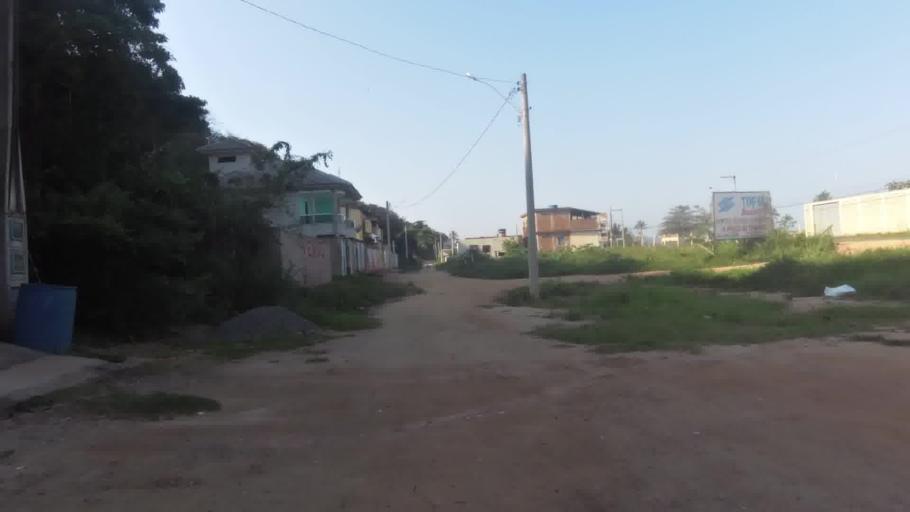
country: BR
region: Espirito Santo
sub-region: Piuma
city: Piuma
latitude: -20.8575
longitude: -40.7550
